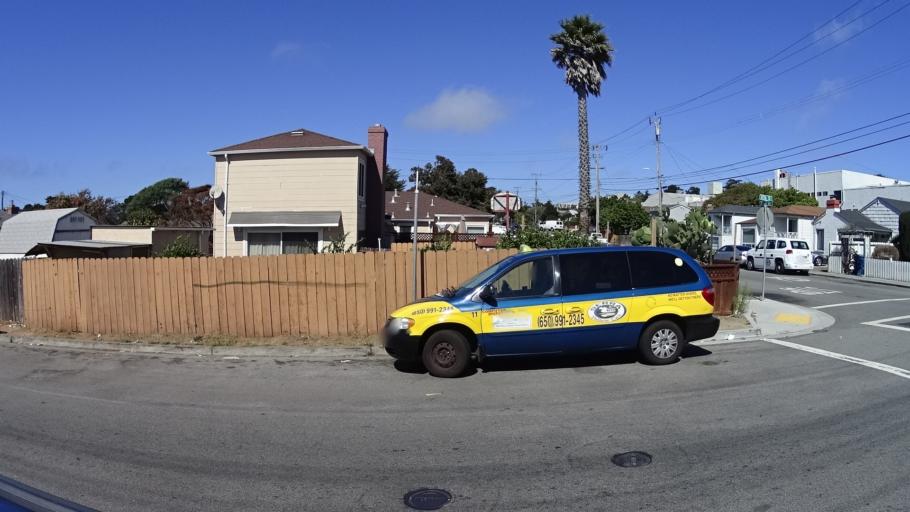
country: US
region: California
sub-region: San Mateo County
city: Broadmoor
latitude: 37.6933
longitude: -122.4724
